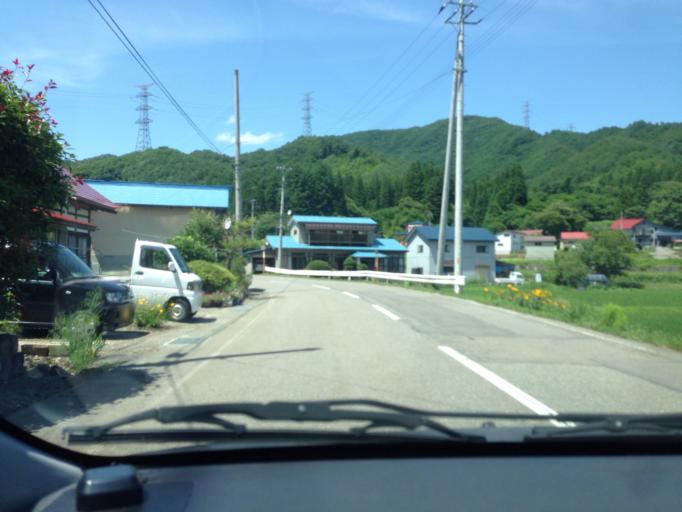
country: JP
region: Tochigi
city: Kuroiso
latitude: 37.2194
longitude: 139.7497
